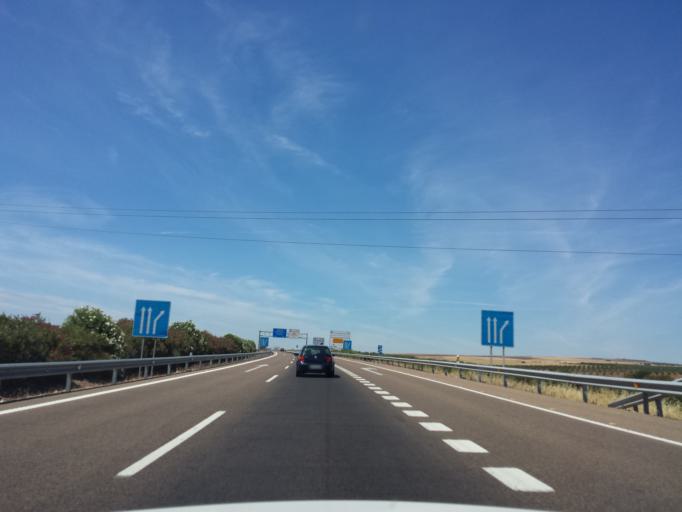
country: ES
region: Extremadura
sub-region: Provincia de Badajoz
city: Trujillanos
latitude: 38.9487
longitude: -6.2748
